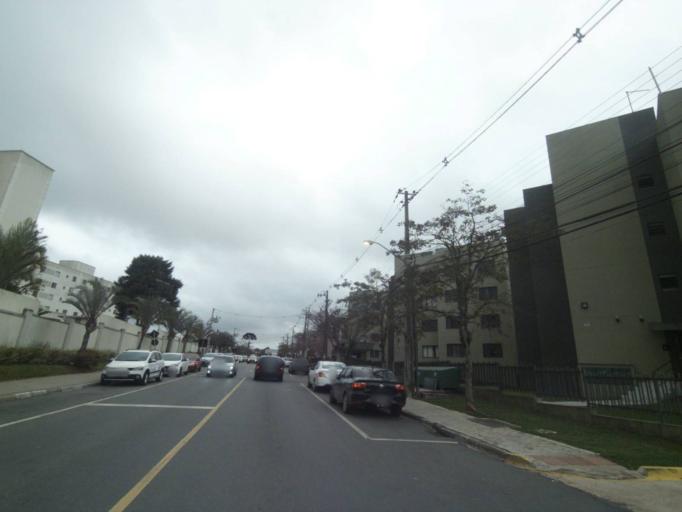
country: BR
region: Parana
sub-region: Curitiba
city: Curitiba
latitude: -25.5091
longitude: -49.2918
